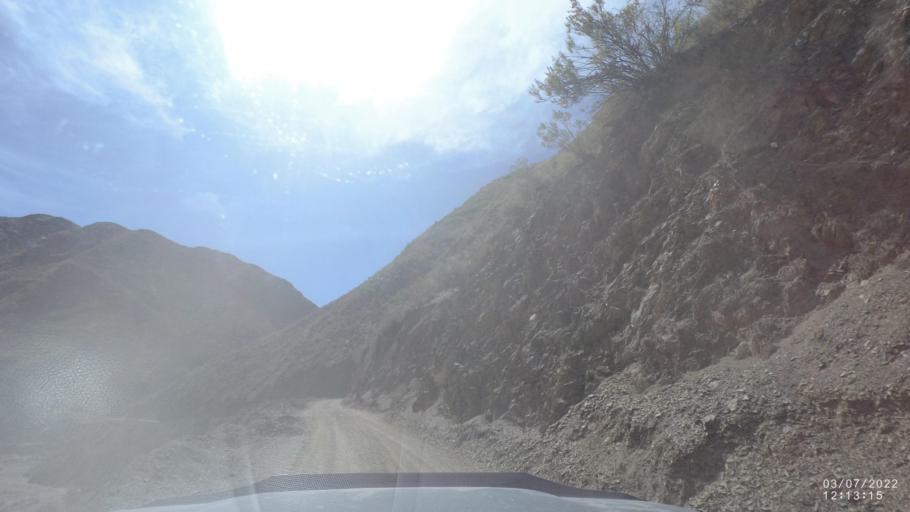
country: BO
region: Cochabamba
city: Irpa Irpa
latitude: -17.8356
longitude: -66.6119
